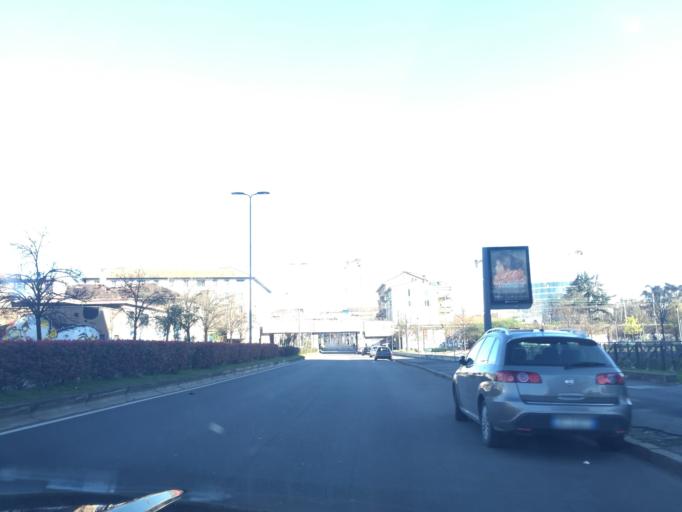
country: IT
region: Lombardy
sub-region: Citta metropolitana di Milano
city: Milano
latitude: 45.4436
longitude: 9.1880
